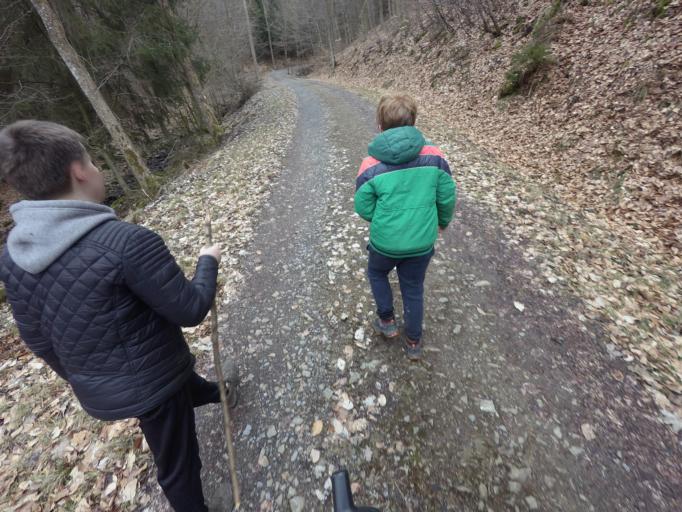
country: BE
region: Wallonia
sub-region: Province de Liege
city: Aywaille
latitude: 50.4337
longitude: 5.7240
